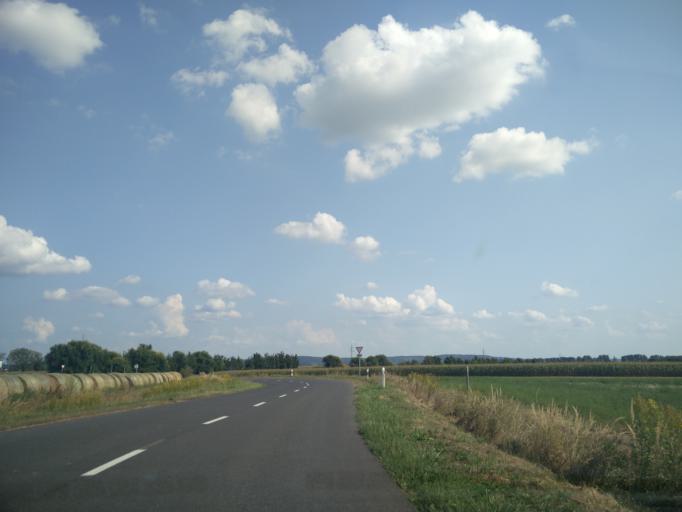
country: HU
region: Zala
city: Zalaegerszeg
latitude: 46.8795
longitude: 16.8283
